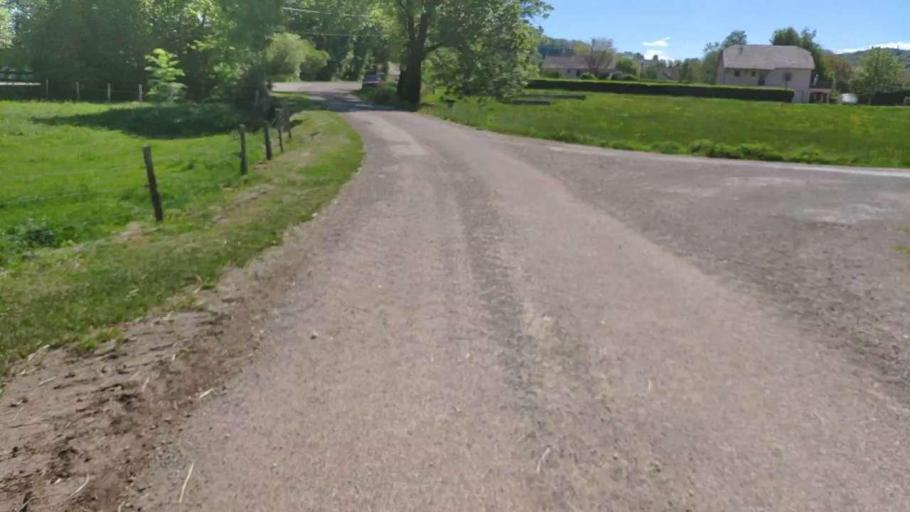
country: FR
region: Franche-Comte
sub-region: Departement du Jura
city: Clairvaux-les-Lacs
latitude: 46.6992
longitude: 5.7218
